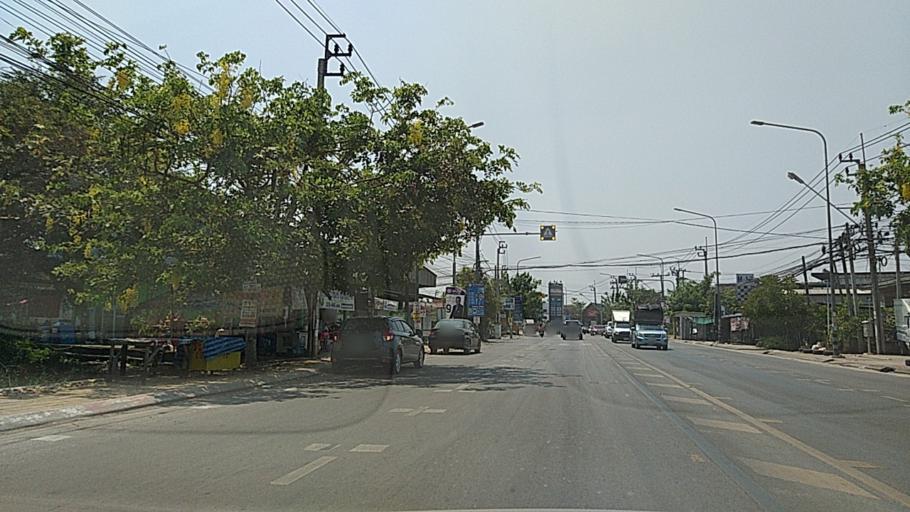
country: TH
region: Nonthaburi
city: Bang Bua Thong
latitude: 13.9097
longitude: 100.3885
